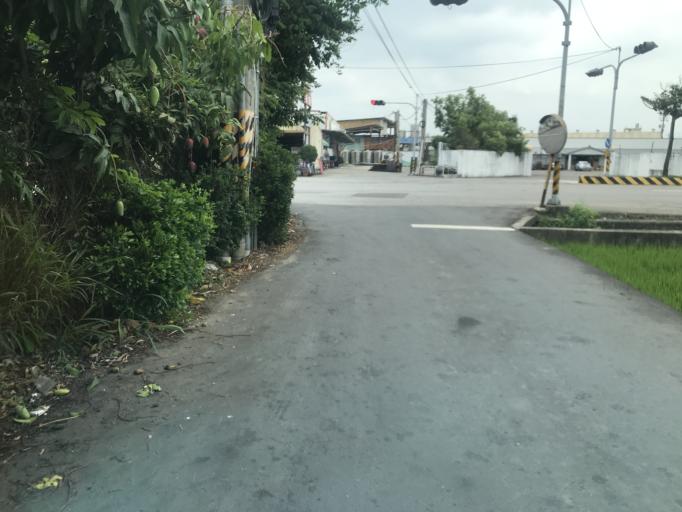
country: TW
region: Taiwan
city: Zhongxing New Village
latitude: 24.0100
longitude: 120.6412
